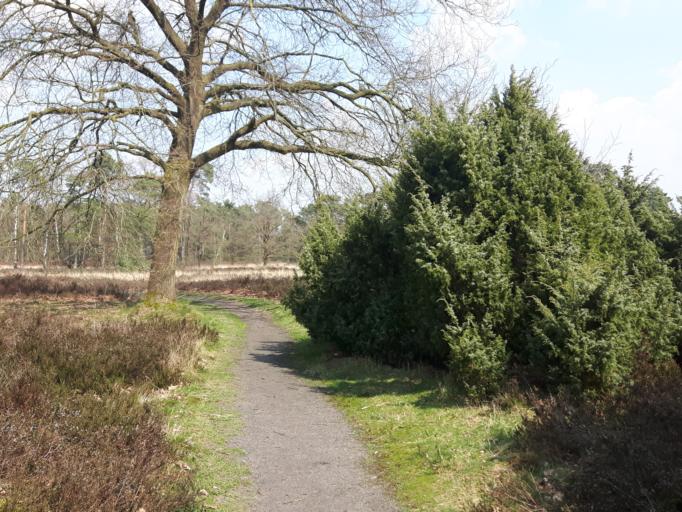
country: NL
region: Overijssel
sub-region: Gemeente Haaksbergen
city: Haaksbergen
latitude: 52.1659
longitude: 6.8094
